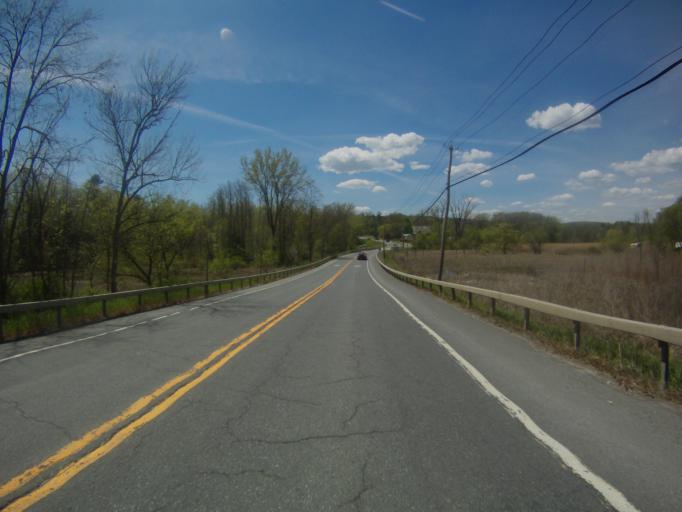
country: US
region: New York
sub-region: Essex County
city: Port Henry
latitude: 43.9577
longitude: -73.4311
